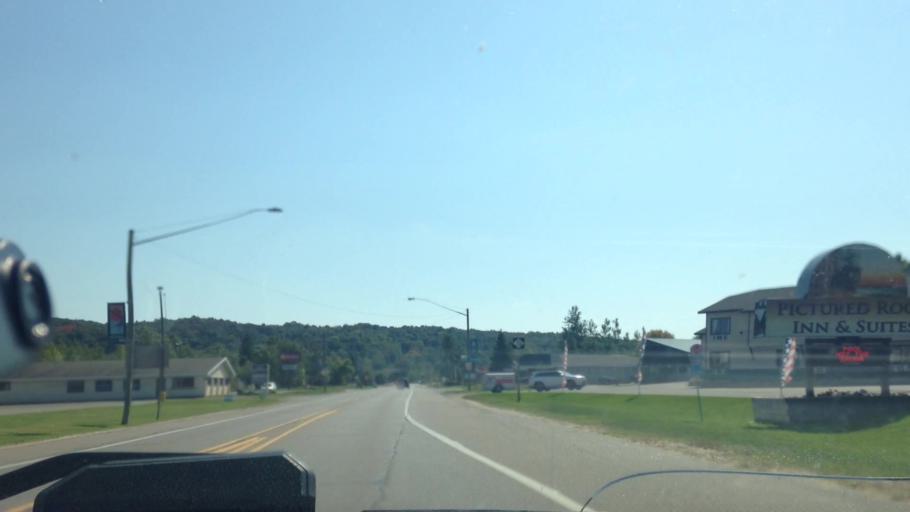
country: US
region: Michigan
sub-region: Alger County
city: Munising
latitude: 46.4067
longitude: -86.6508
